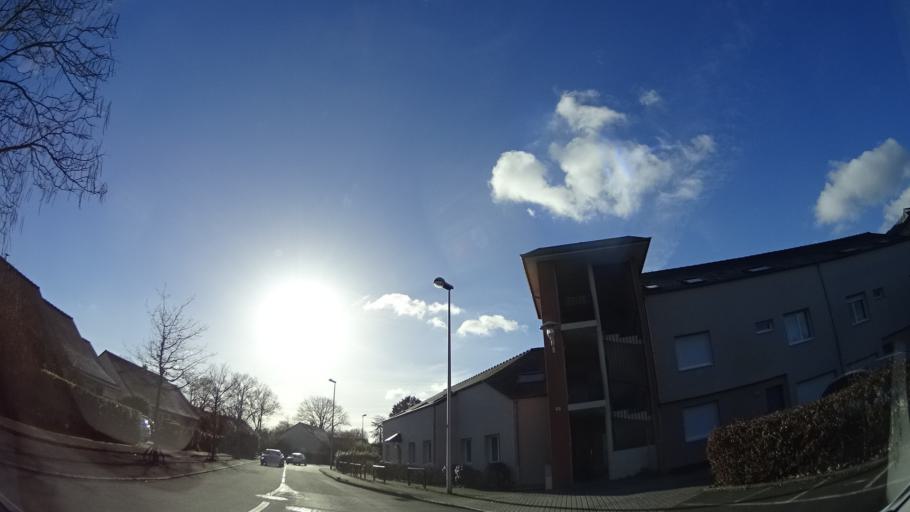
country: FR
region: Brittany
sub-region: Departement d'Ille-et-Vilaine
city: Betton
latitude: 48.1753
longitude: -1.6373
